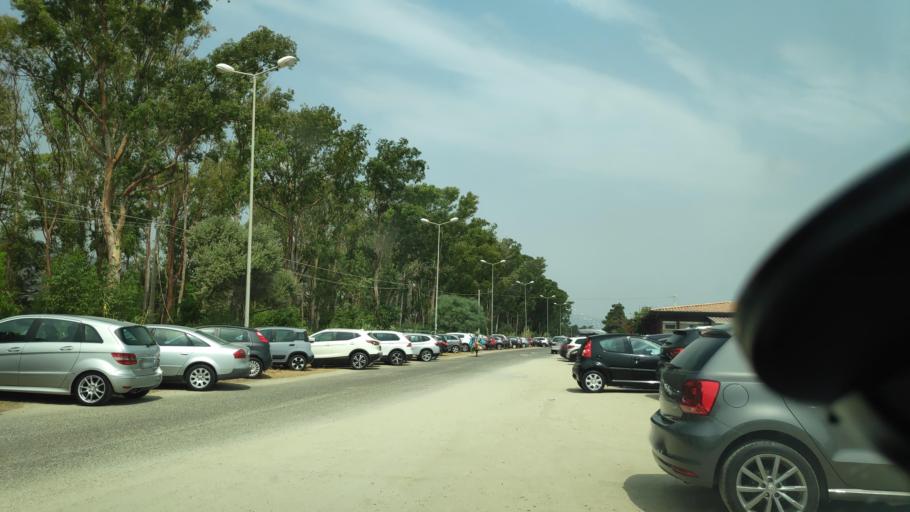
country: IT
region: Calabria
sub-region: Provincia di Catanzaro
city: Isca Marina
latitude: 38.6140
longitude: 16.5616
